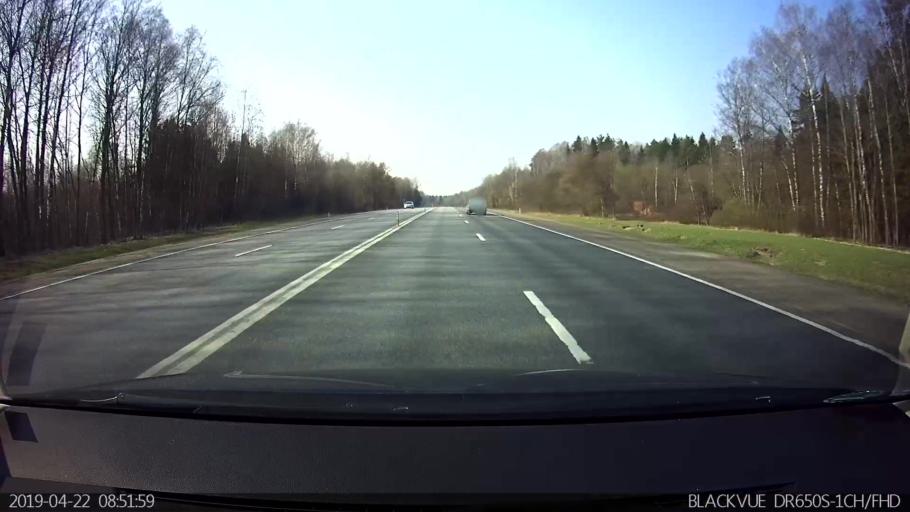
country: RU
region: Smolensk
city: Pechersk
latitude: 54.9162
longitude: 32.1330
